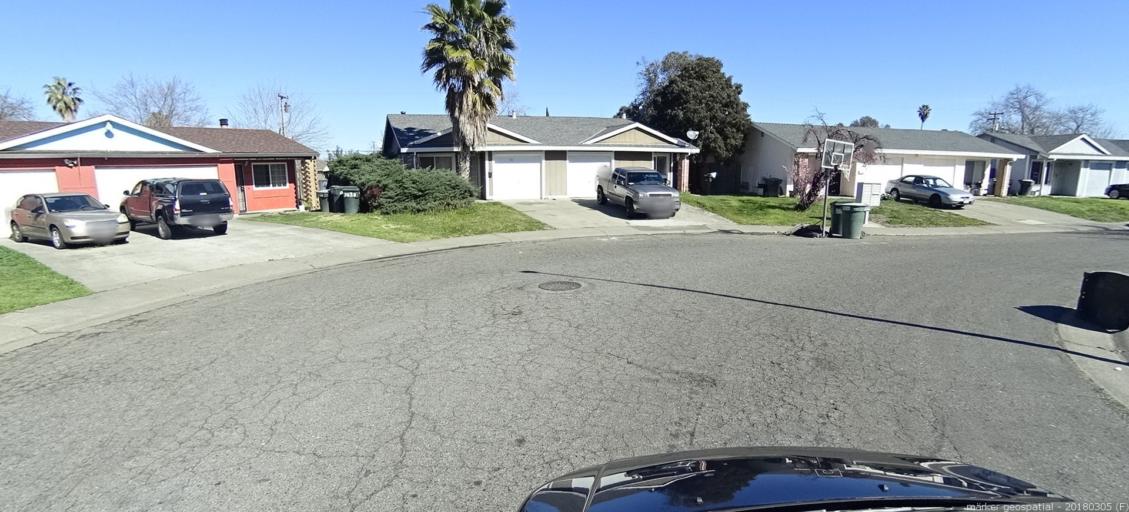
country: US
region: California
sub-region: Sacramento County
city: Florin
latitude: 38.4911
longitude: -121.4120
